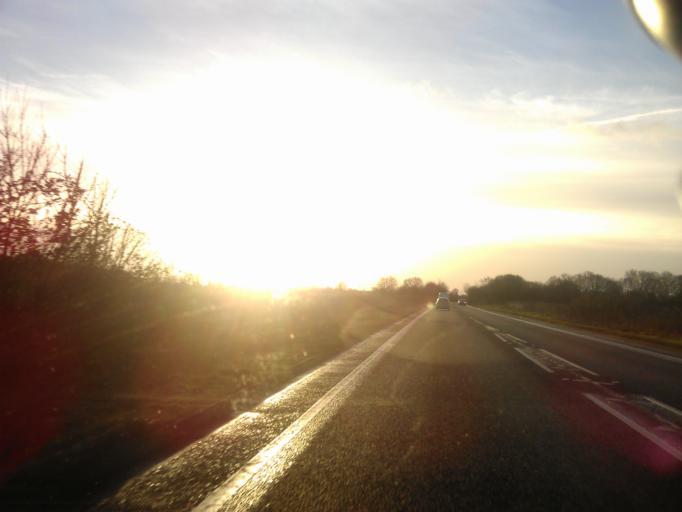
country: GB
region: England
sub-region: Essex
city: Little Clacton
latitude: 51.8323
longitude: 1.1280
